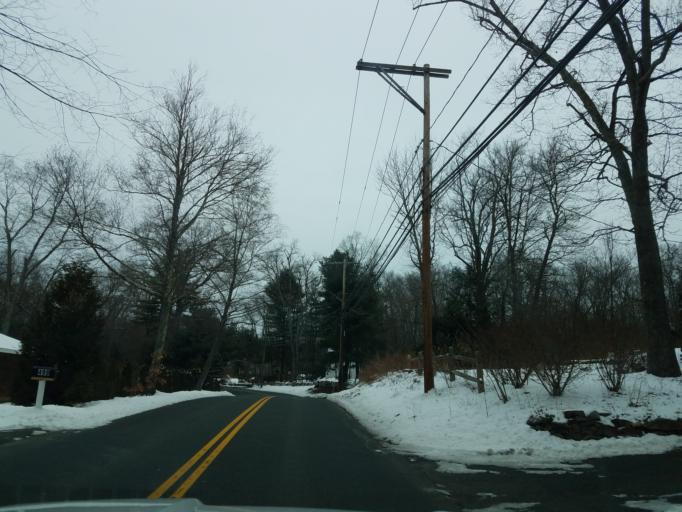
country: US
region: Connecticut
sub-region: Hartford County
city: Collinsville
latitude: 41.7757
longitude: -72.9008
